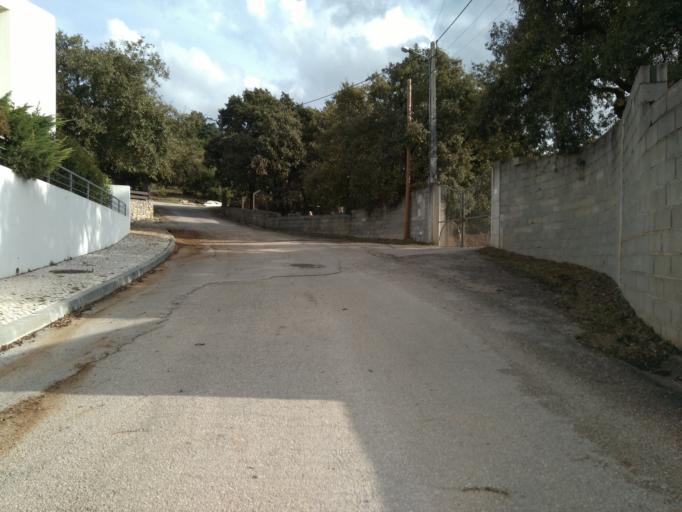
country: PT
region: Leiria
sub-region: Porto de Mos
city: Porto de Mos
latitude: 39.5954
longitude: -8.8065
